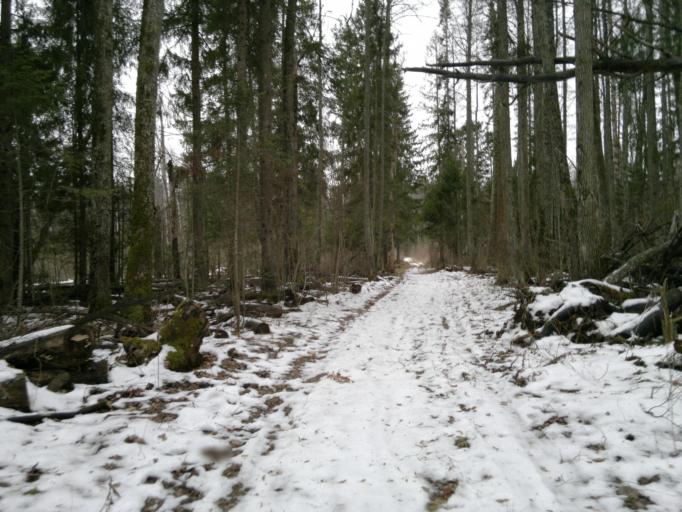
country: RU
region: Mariy-El
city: Yoshkar-Ola
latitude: 56.6076
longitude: 47.9601
